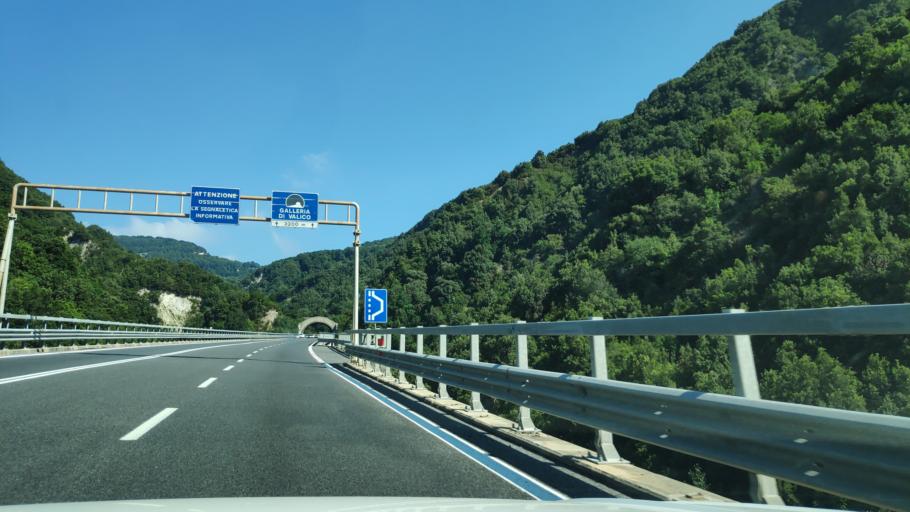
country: IT
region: Calabria
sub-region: Provincia di Reggio Calabria
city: Amato
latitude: 38.3679
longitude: 16.1840
